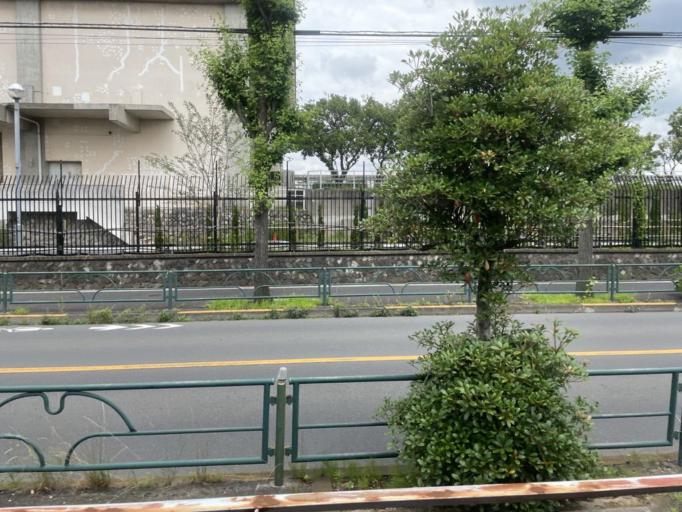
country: JP
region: Chiba
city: Matsudo
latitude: 35.7615
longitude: 139.8743
